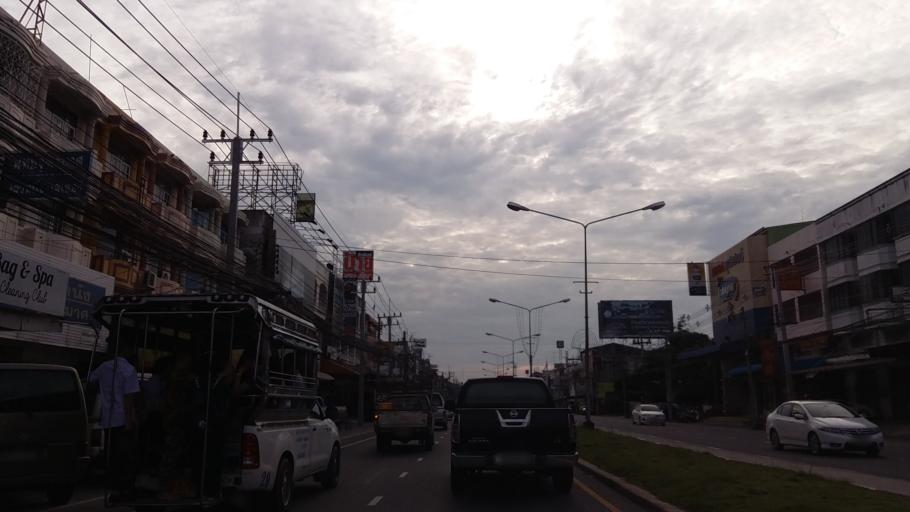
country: TH
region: Chon Buri
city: Chon Buri
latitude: 13.3439
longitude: 100.9652
